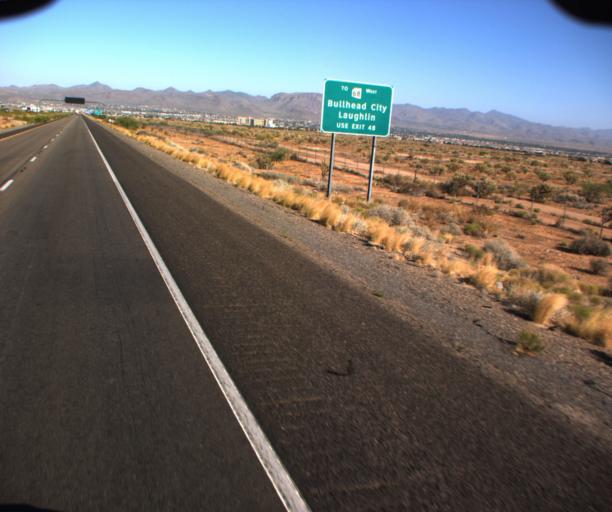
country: US
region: Arizona
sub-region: Mohave County
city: New Kingman-Butler
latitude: 35.2116
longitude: -113.9708
